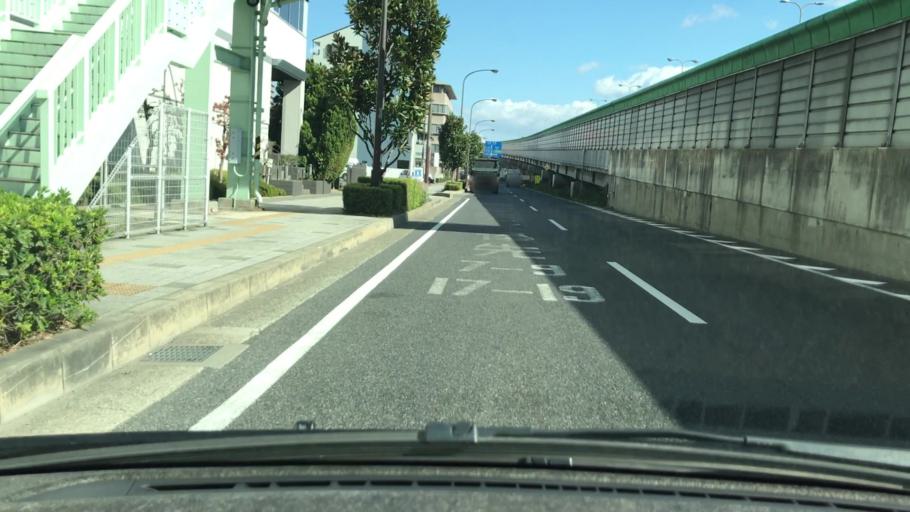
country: JP
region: Hyogo
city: Kobe
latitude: 34.7033
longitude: 135.2213
